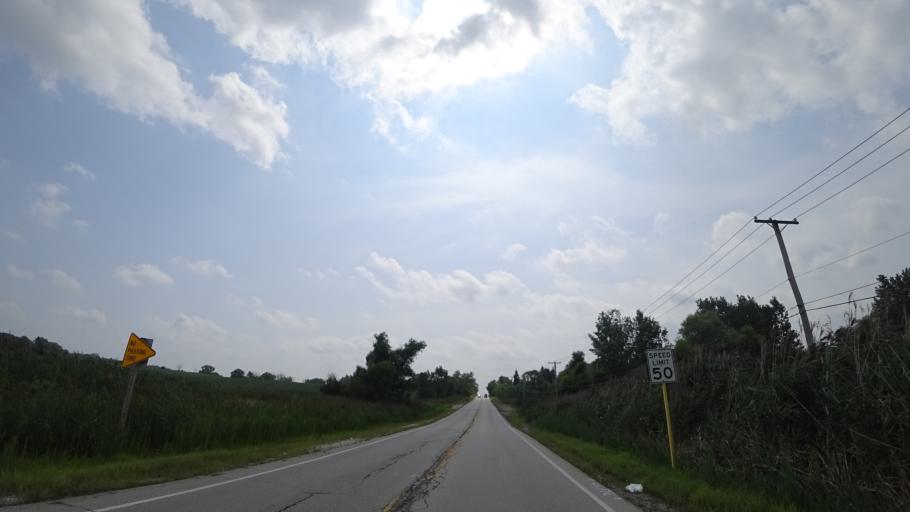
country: US
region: Illinois
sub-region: Cook County
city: Orland Park
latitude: 41.6222
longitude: -87.8921
